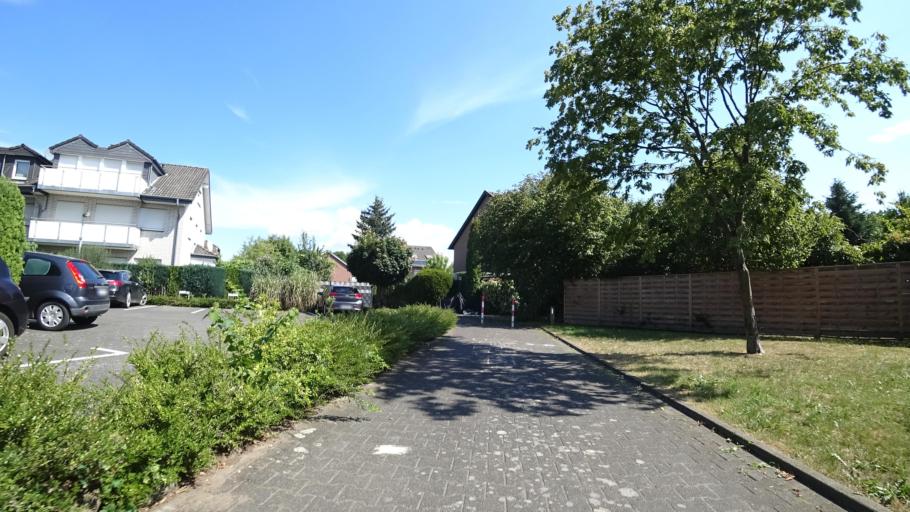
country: DE
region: North Rhine-Westphalia
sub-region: Regierungsbezirk Detmold
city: Steinhagen
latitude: 51.9541
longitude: 8.3962
